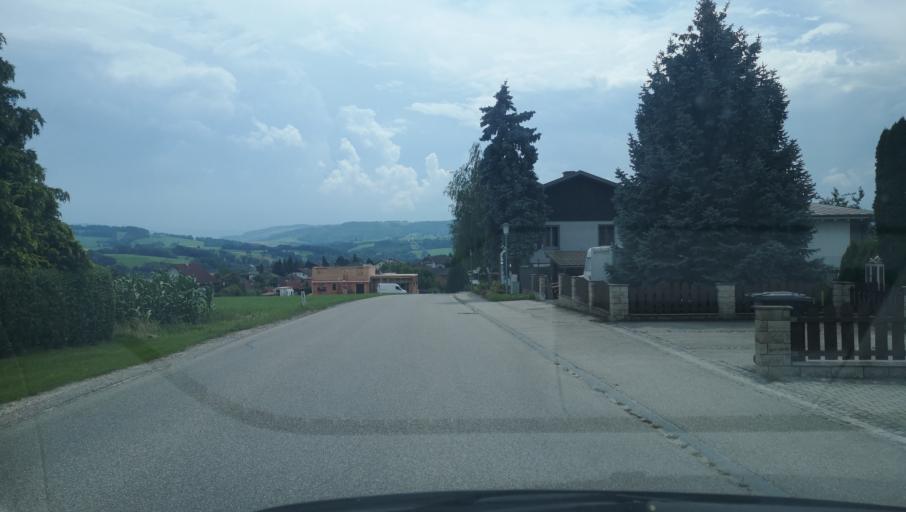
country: AT
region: Lower Austria
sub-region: Politischer Bezirk Amstetten
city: Ferschnitz
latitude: 48.0992
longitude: 14.9793
